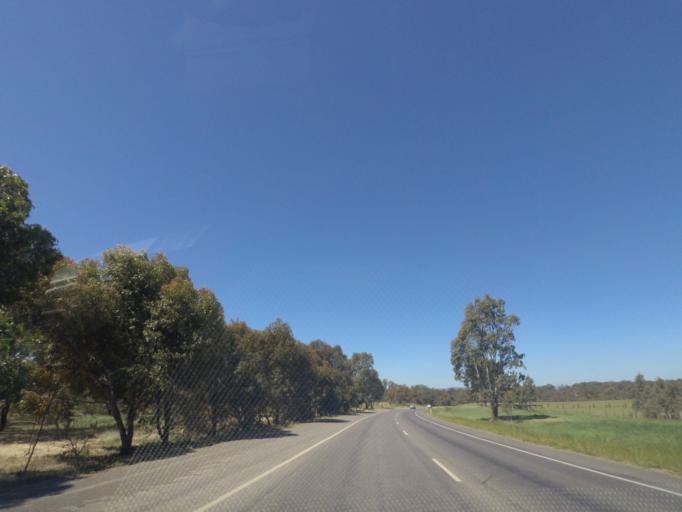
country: AU
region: Victoria
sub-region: Murrindindi
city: Kinglake West
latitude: -37.0292
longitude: 145.0902
